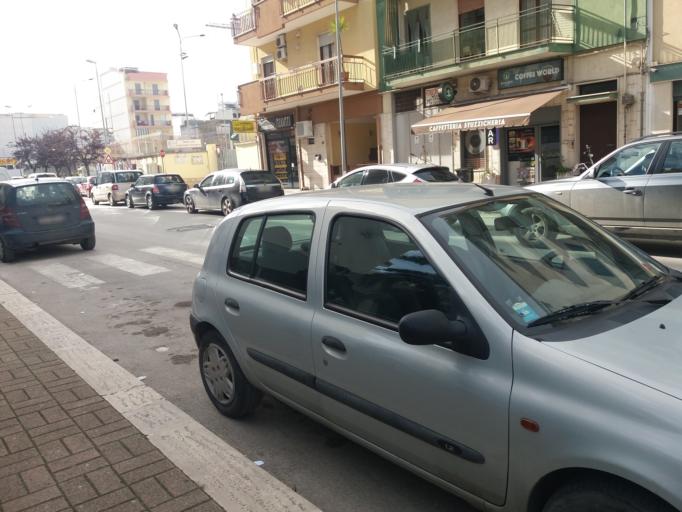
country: IT
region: Apulia
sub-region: Provincia di Barletta - Andria - Trani
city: Andria
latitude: 41.2363
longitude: 16.2947
